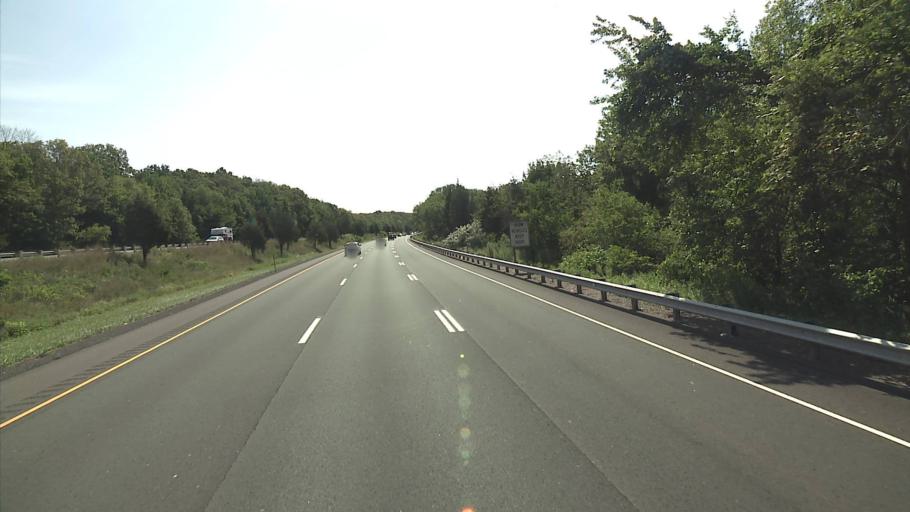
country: US
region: Connecticut
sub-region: Hartford County
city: Terramuggus
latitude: 41.6487
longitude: -72.4766
